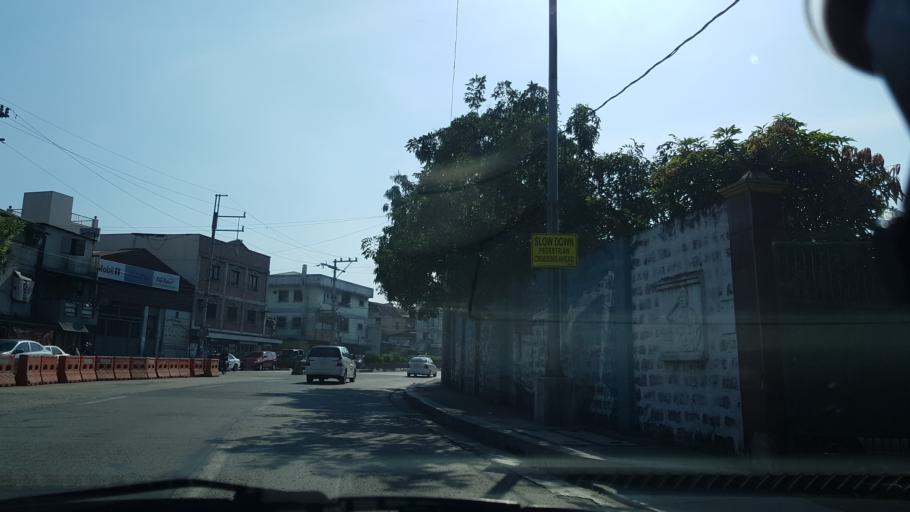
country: PH
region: Metro Manila
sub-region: Marikina
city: Calumpang
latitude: 14.6168
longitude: 121.0768
